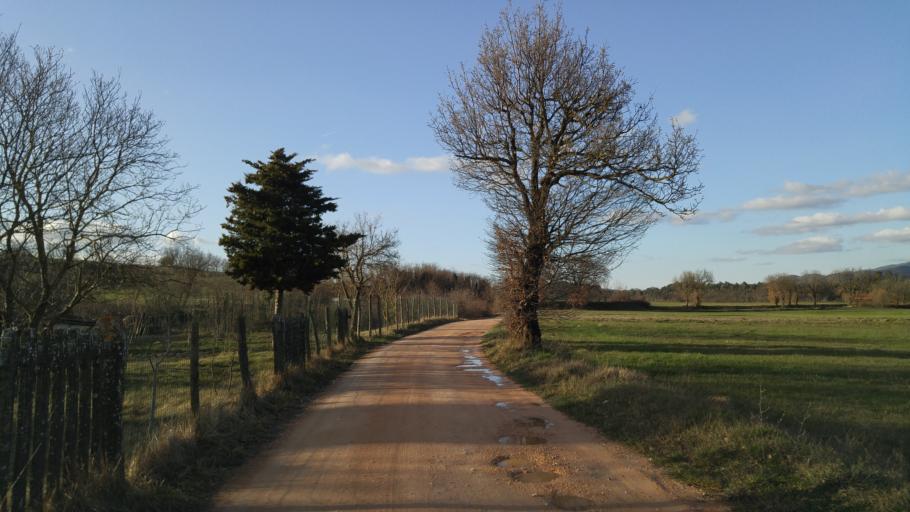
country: IT
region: The Marches
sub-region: Provincia di Pesaro e Urbino
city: Cagli
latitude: 43.5328
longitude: 12.6937
